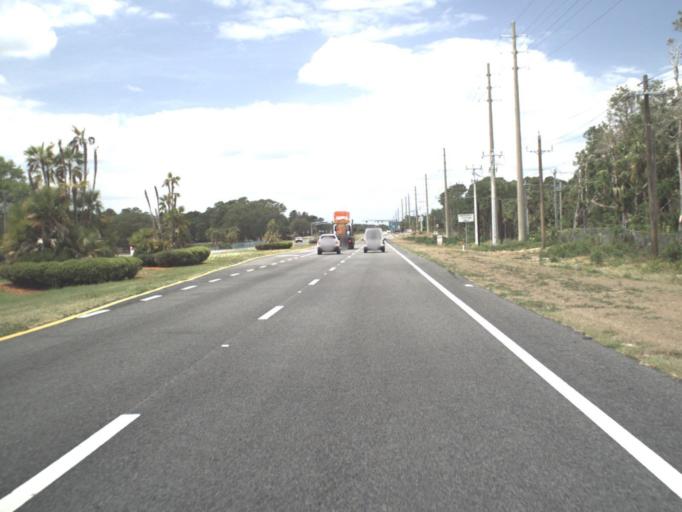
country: US
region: Florida
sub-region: Brevard County
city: Port Saint John
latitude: 28.5290
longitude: -80.8052
